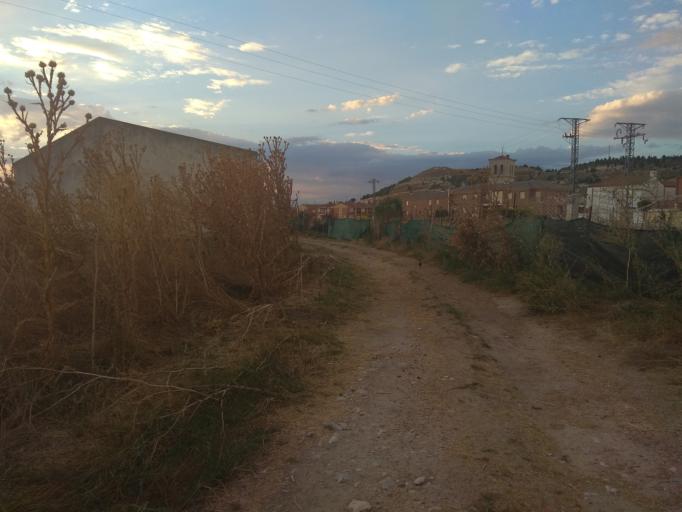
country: ES
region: Castille and Leon
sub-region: Provincia de Valladolid
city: Portillo
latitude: 41.4710
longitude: -4.5939
